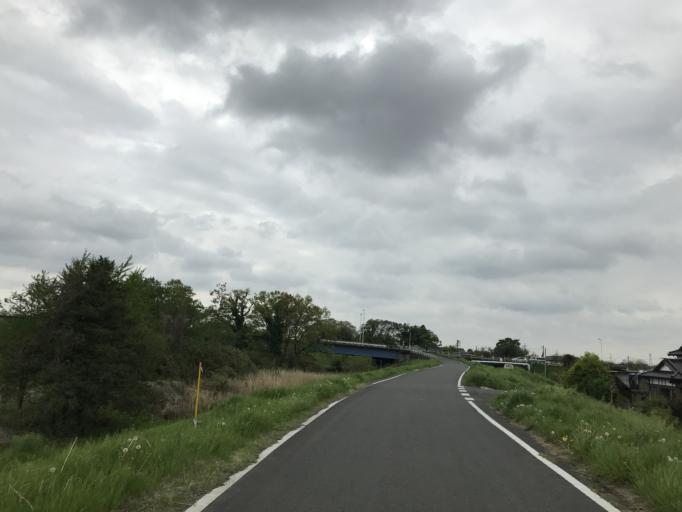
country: JP
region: Ibaraki
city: Mitsukaido
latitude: 36.0410
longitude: 140.0252
